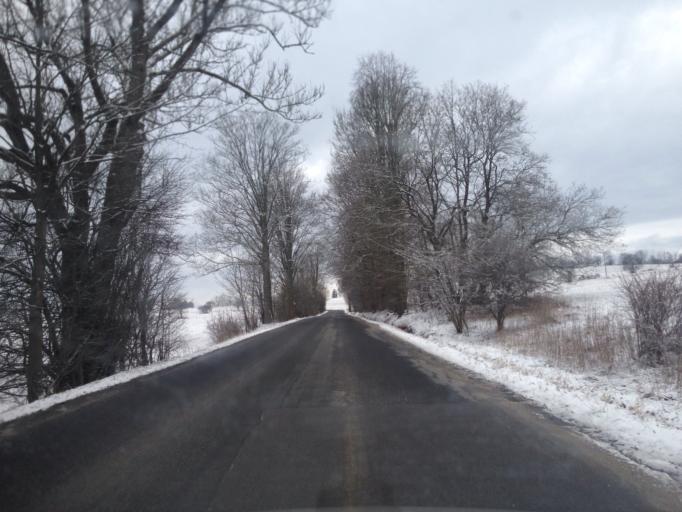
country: CZ
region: Liberecky
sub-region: Okres Semily
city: Ponikla
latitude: 50.6469
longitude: 15.4300
